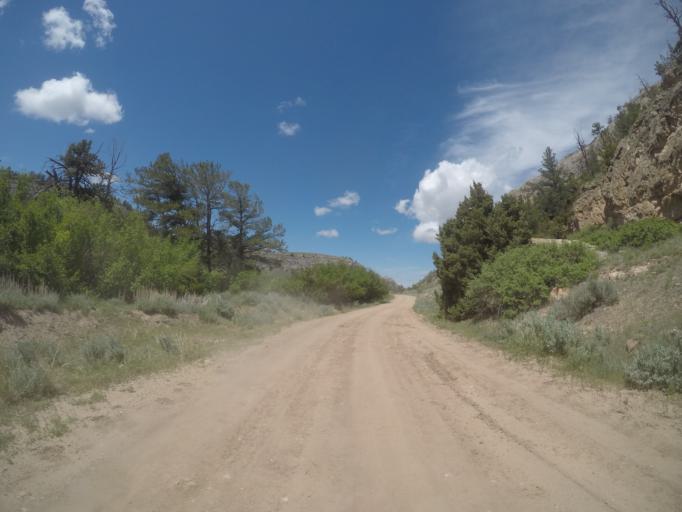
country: US
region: Wyoming
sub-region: Big Horn County
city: Lovell
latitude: 45.2232
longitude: -108.5942
